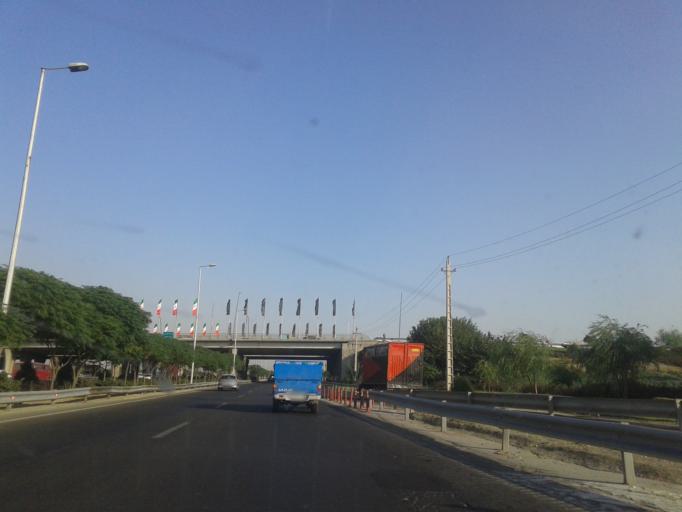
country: IR
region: Tehran
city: Eslamshahr
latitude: 35.6506
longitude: 51.2718
